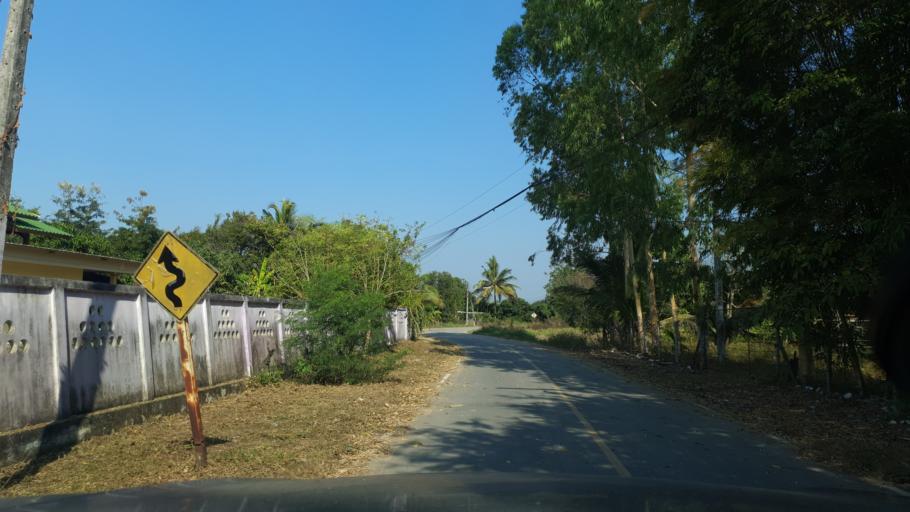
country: TH
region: Chiang Mai
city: Saraphi
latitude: 18.6934
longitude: 99.0863
